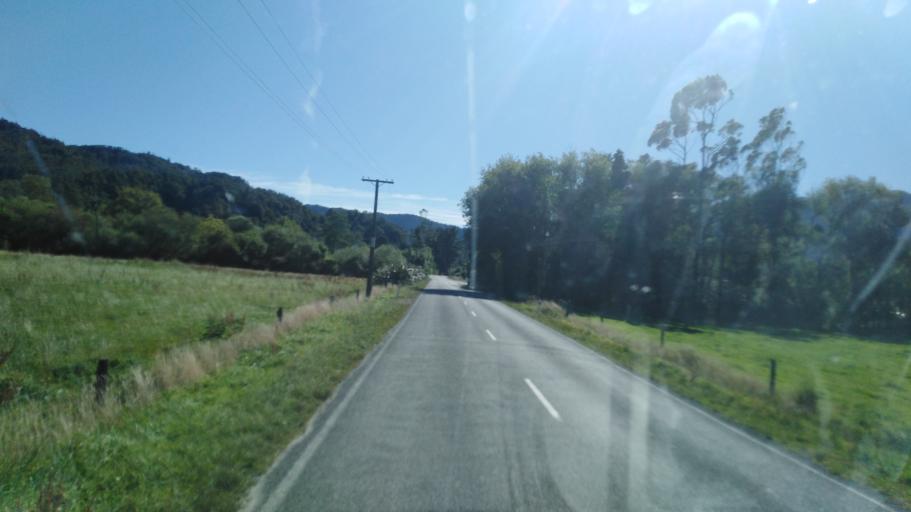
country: NZ
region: West Coast
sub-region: Buller District
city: Westport
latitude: -41.5311
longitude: 171.9642
